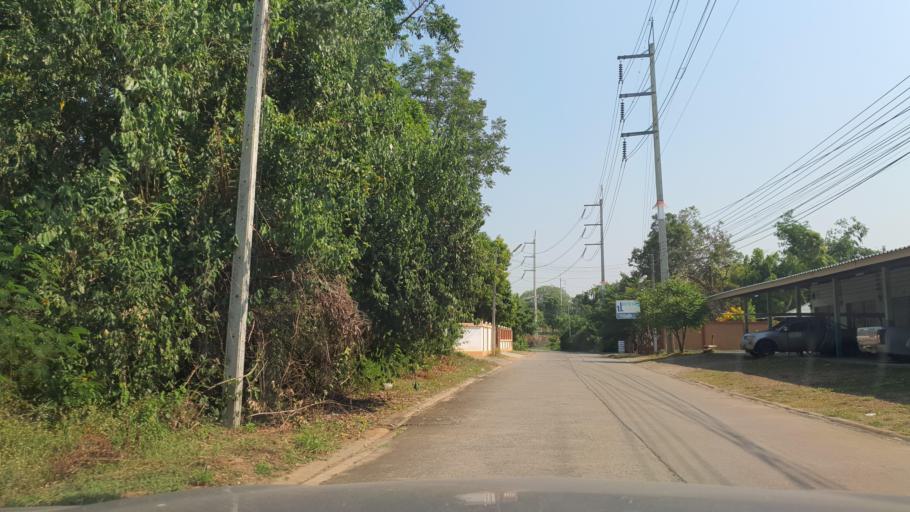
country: TH
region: Kanchanaburi
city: Kanchanaburi
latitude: 14.0669
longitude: 99.4859
